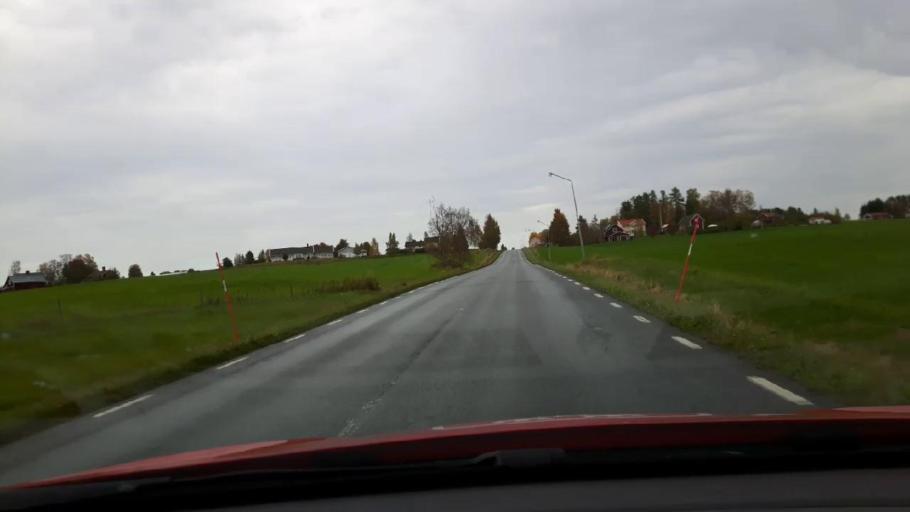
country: SE
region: Jaemtland
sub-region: Bergs Kommun
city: Hoverberg
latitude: 63.0054
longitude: 14.3400
